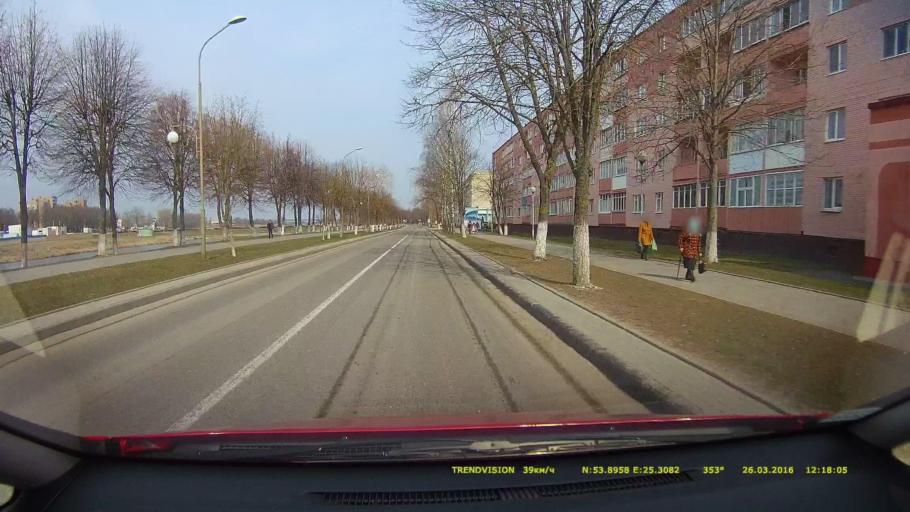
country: BY
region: Grodnenskaya
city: Lida
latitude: 53.8958
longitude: 25.3082
